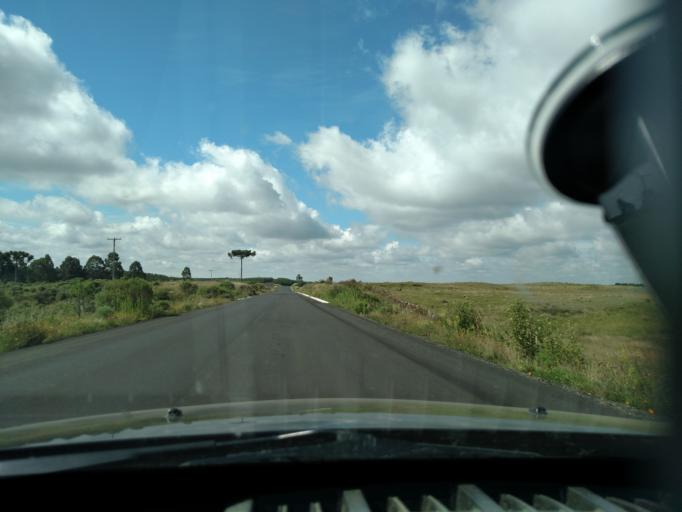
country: BR
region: Santa Catarina
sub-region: Lages
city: Lages
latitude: -27.9907
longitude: -50.0895
